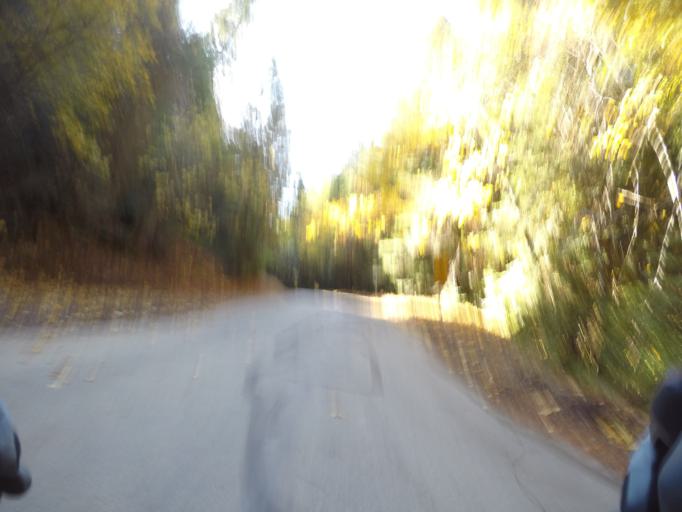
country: US
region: California
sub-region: Santa Clara County
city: Lexington Hills
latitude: 37.1537
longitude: -122.0141
